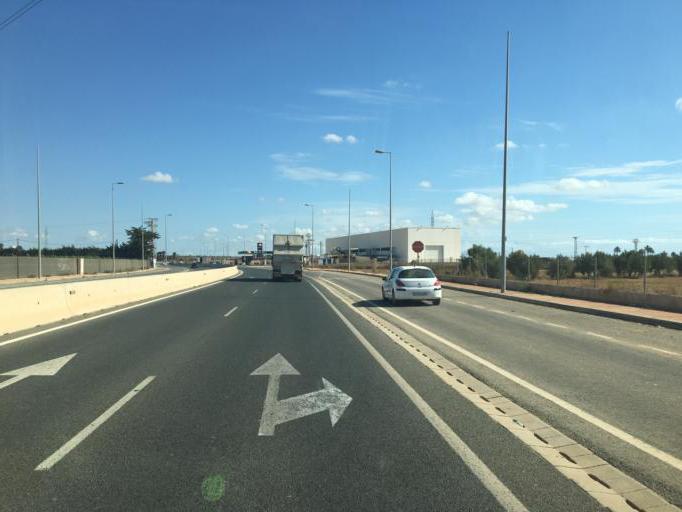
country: ES
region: Murcia
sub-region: Murcia
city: Cartagena
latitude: 37.6518
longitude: -0.9831
